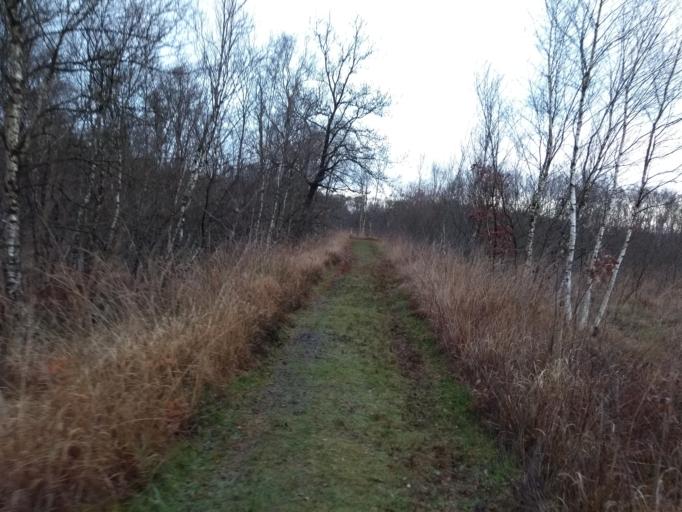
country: NL
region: Overijssel
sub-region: Gemeente Twenterand
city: Westerhaar-Vriezenveensewijk
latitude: 52.4494
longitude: 6.6730
